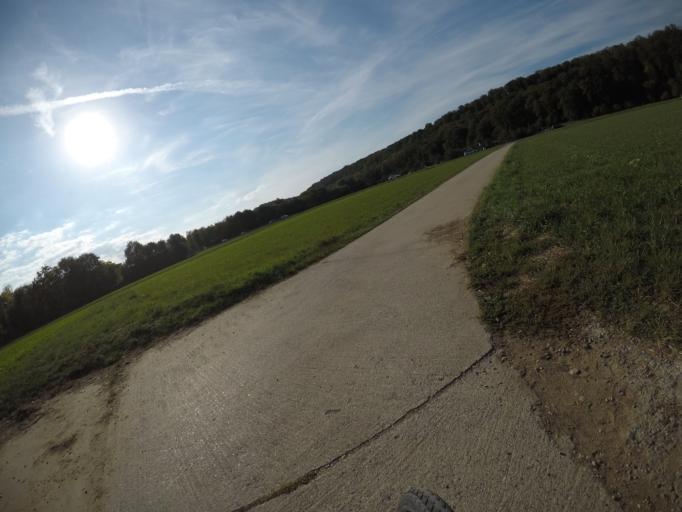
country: DE
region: Baden-Wuerttemberg
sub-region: Regierungsbezirk Stuttgart
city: Neckartenzlingen
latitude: 48.5982
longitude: 9.2485
